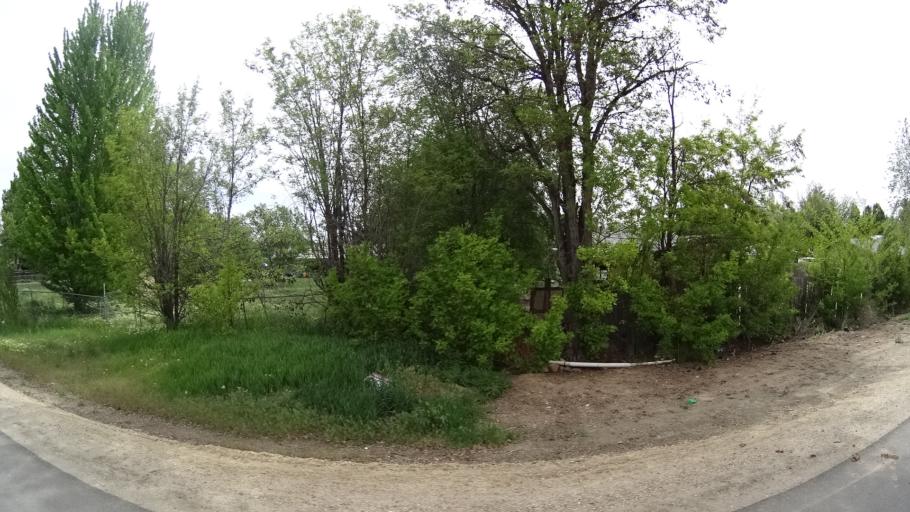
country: US
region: Idaho
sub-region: Ada County
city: Meridian
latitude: 43.5413
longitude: -116.3144
